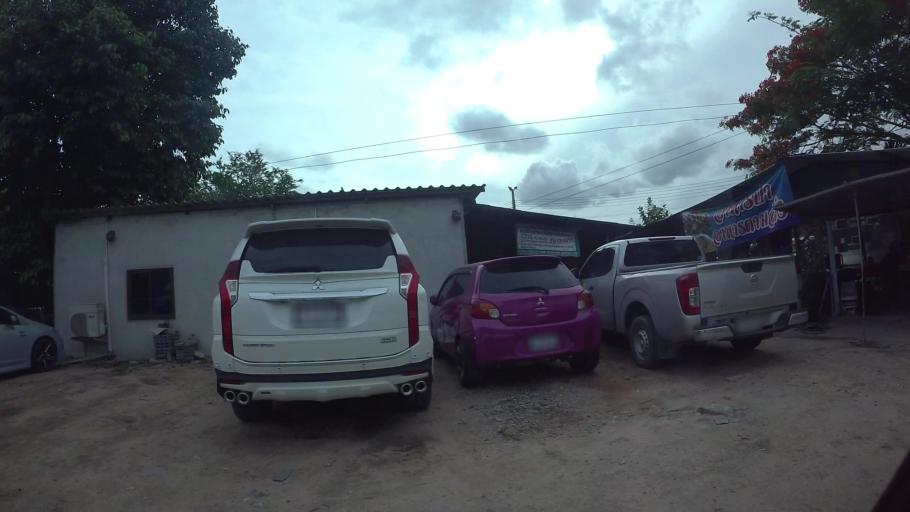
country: TH
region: Chon Buri
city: Ban Talat Bueng
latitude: 13.1222
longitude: 100.9723
